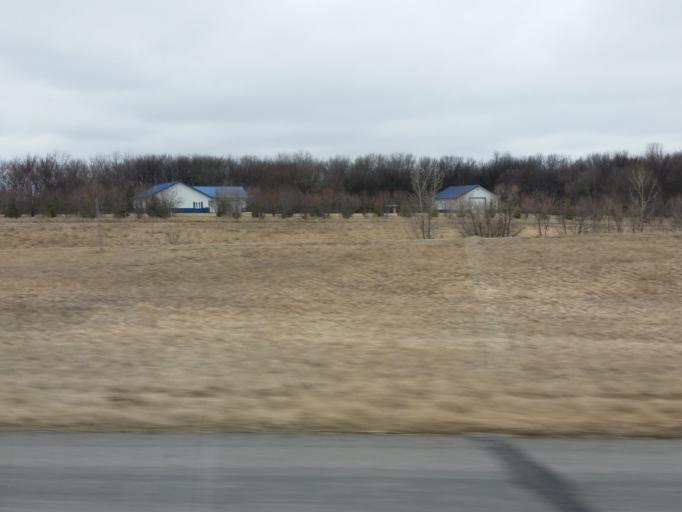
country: US
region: North Dakota
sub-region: Cass County
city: Horace
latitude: 46.5415
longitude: -96.8255
